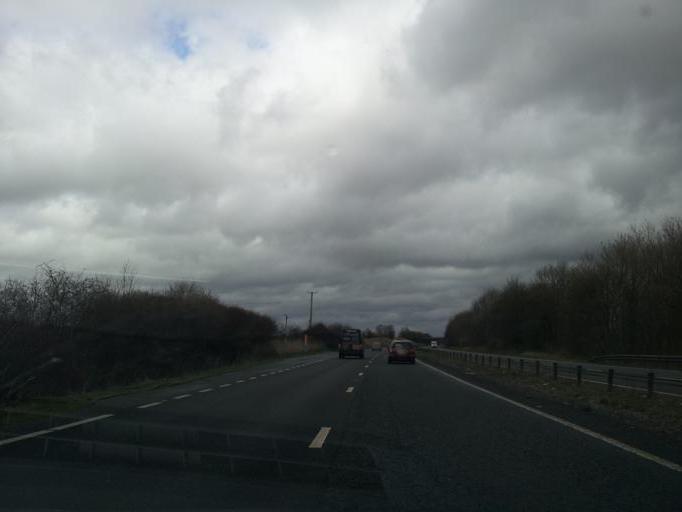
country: GB
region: England
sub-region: Somerset
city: Ilchester
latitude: 51.0093
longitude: -2.6885
